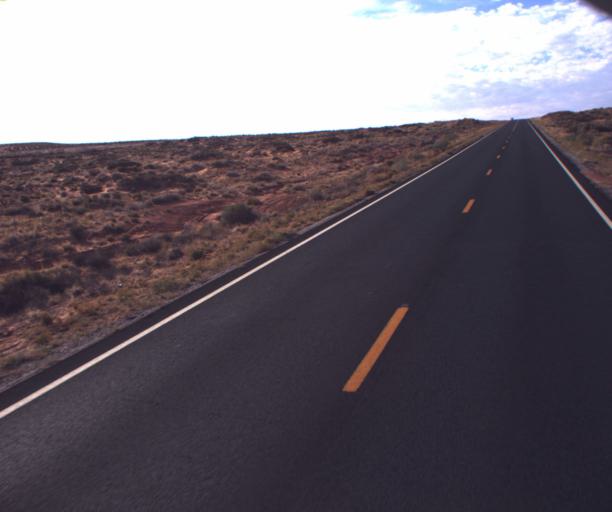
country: US
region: Arizona
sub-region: Apache County
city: Many Farms
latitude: 36.8985
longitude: -109.6257
